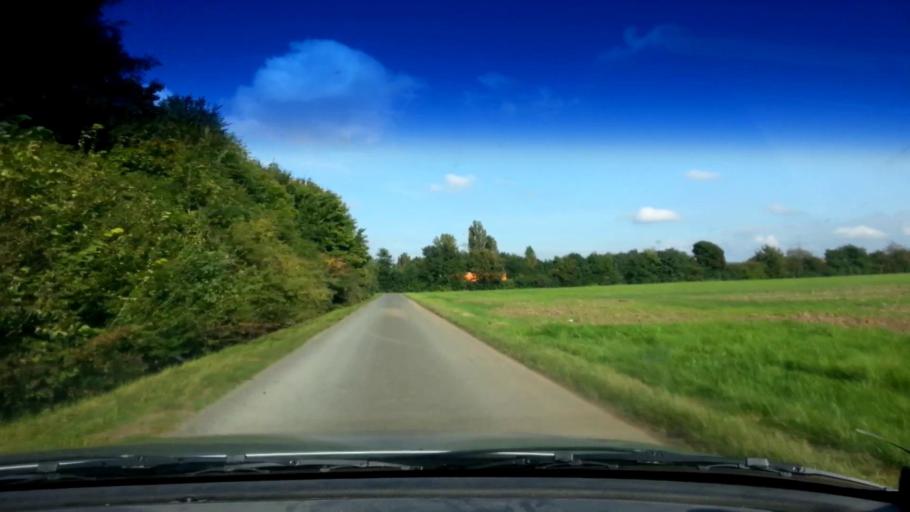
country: DE
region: Bavaria
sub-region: Upper Franconia
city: Viereth-Trunstadt
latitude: 49.9308
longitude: 10.7779
